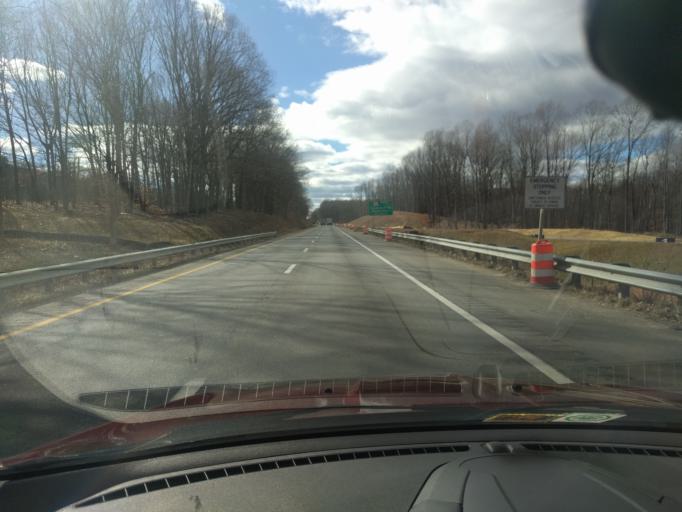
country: US
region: Virginia
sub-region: City of Lynchburg
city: West Lynchburg
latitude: 37.3723
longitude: -79.1499
